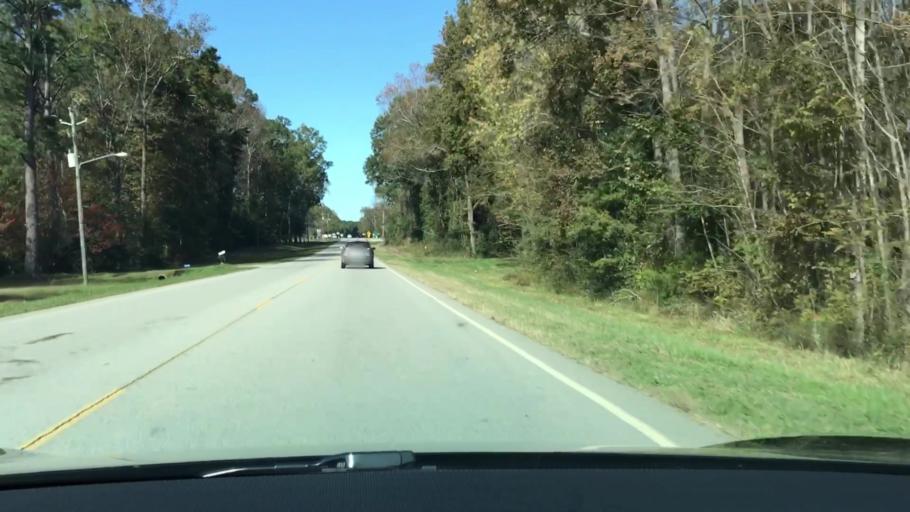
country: US
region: Georgia
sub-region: Warren County
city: Firing Range
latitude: 33.4599
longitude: -82.7032
